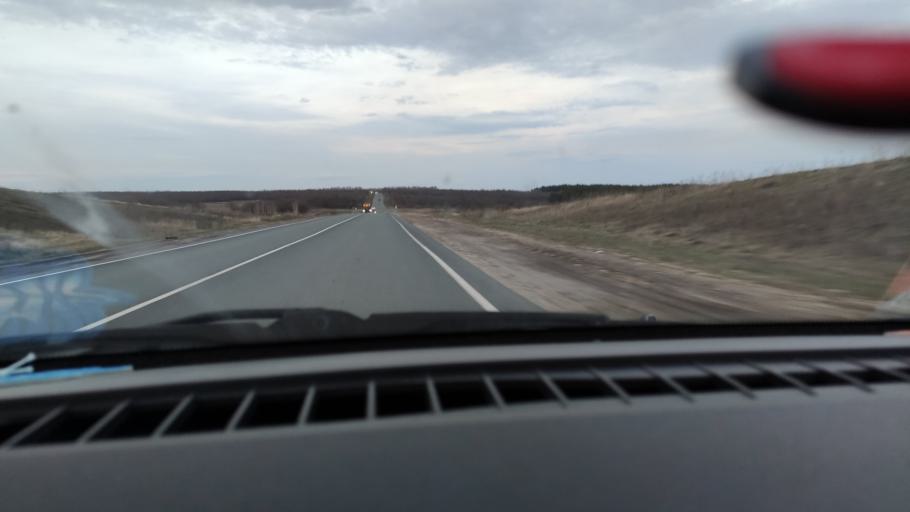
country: RU
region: Saratov
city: Sinodskoye
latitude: 51.9309
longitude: 46.5792
